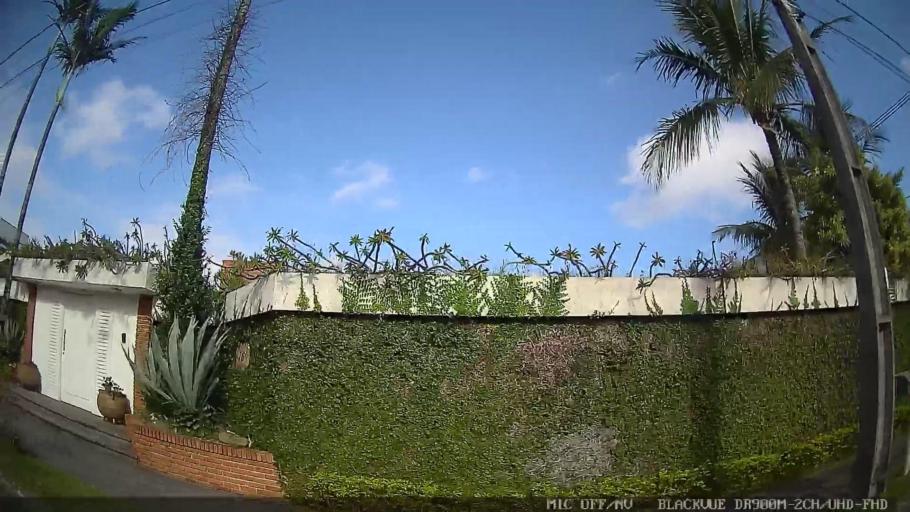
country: BR
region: Sao Paulo
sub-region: Peruibe
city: Peruibe
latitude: -24.3114
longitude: -46.9915
